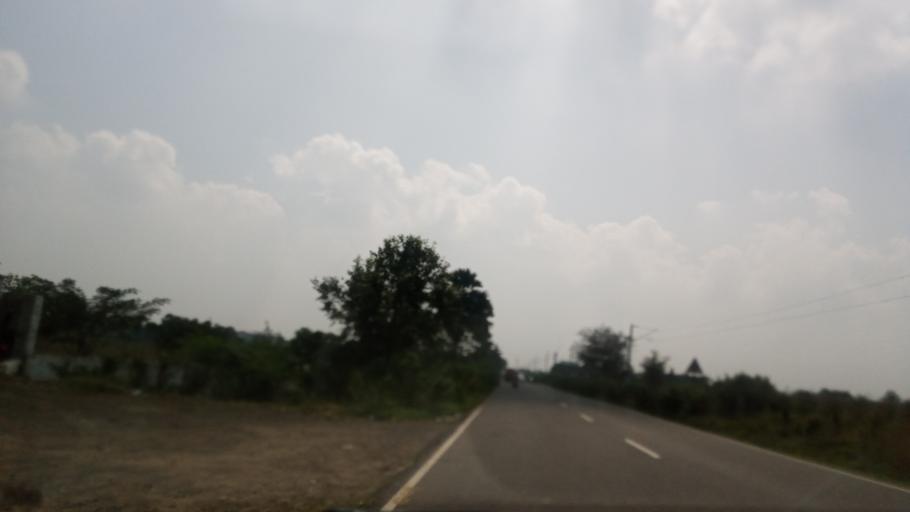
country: IN
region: Tamil Nadu
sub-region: Kancheepuram
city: Kanchipuram
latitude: 12.8845
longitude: 79.6882
